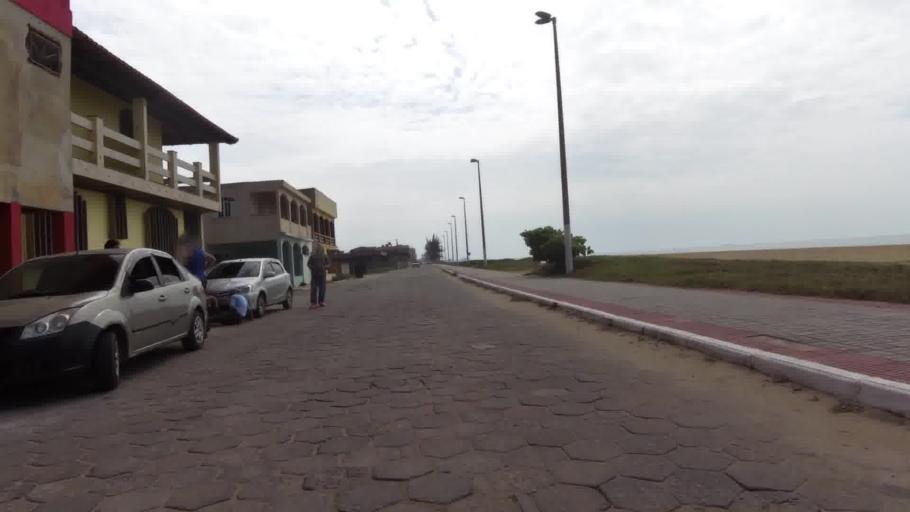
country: BR
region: Espirito Santo
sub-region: Marataizes
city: Marataizes
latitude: -21.0313
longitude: -40.8128
